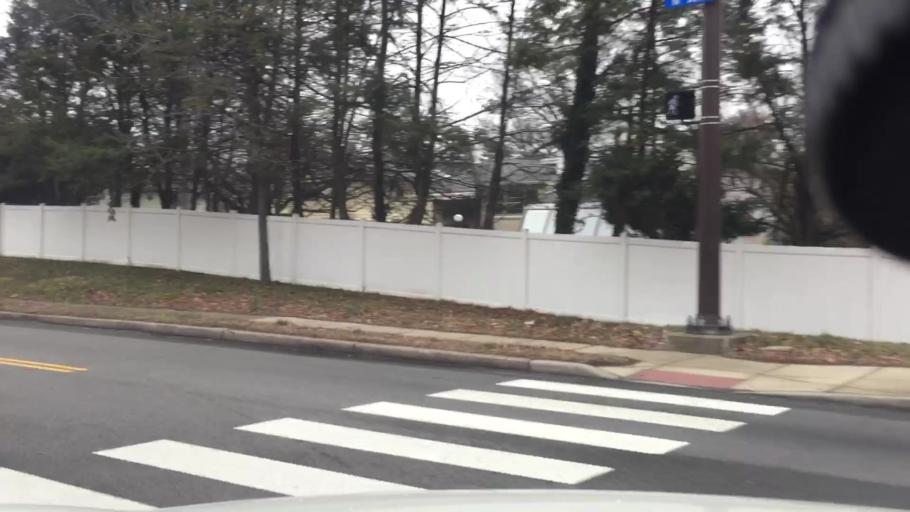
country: US
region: Pennsylvania
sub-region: Montgomery County
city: Wyndmoor
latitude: 40.0732
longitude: -75.1894
